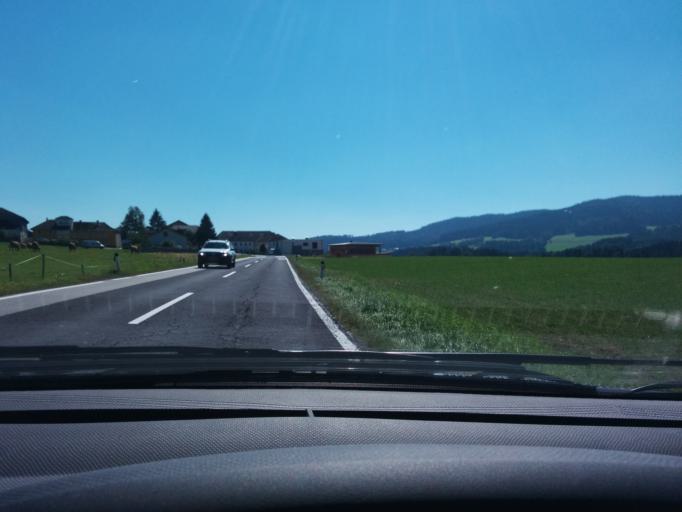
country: AT
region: Upper Austria
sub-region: Politischer Bezirk Rohrbach
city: Ulrichsberg
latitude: 48.6726
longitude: 13.9259
